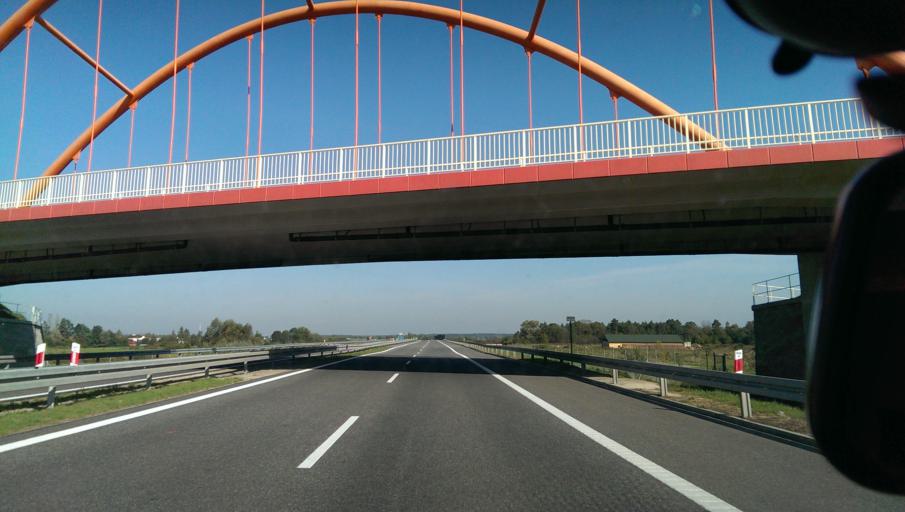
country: PL
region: Subcarpathian Voivodeship
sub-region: Powiat rzeszowski
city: Rudna Wielka
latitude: 50.0885
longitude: 21.9333
